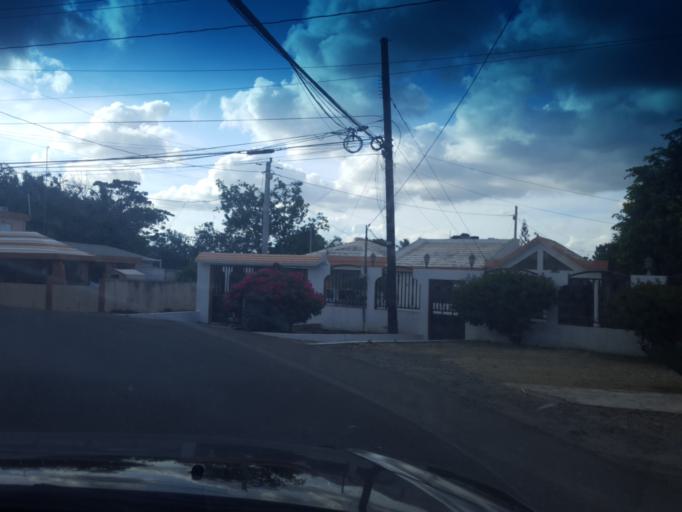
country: DO
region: Santiago
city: Licey al Medio
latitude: 19.3739
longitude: -70.6374
